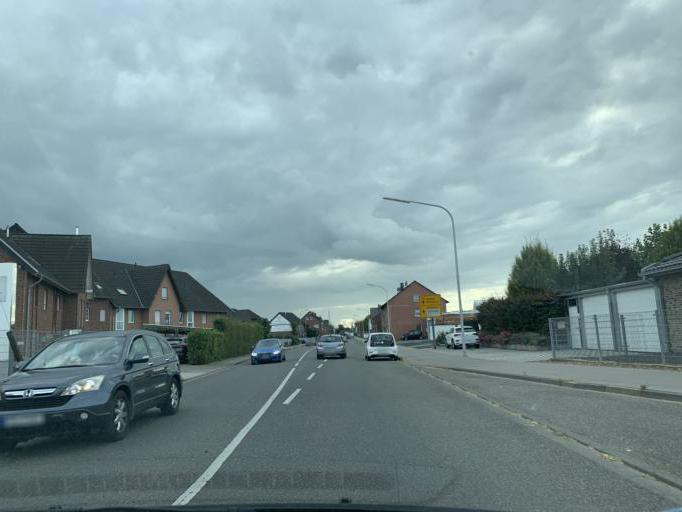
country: DE
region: North Rhine-Westphalia
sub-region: Regierungsbezirk Koln
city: Wassenberg
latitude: 51.0773
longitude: 6.1344
